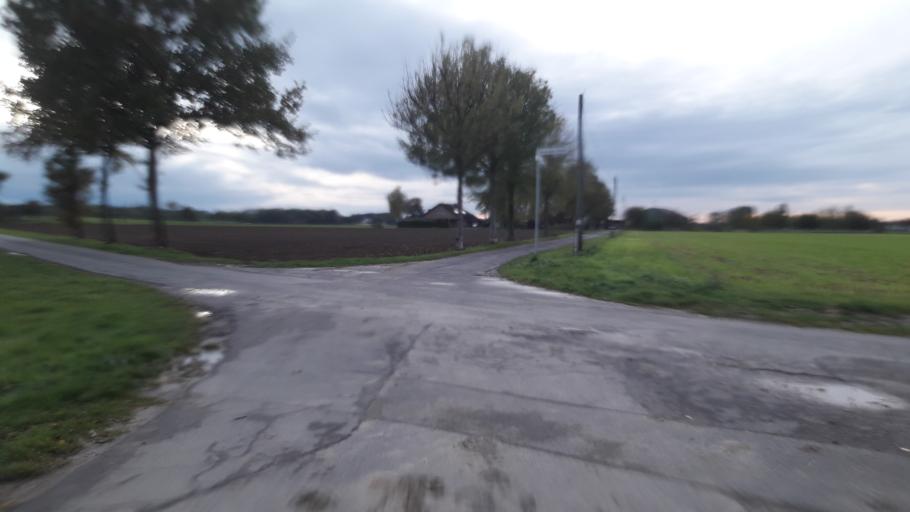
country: DE
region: North Rhine-Westphalia
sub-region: Regierungsbezirk Detmold
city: Hovelhof
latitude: 51.7355
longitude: 8.6562
